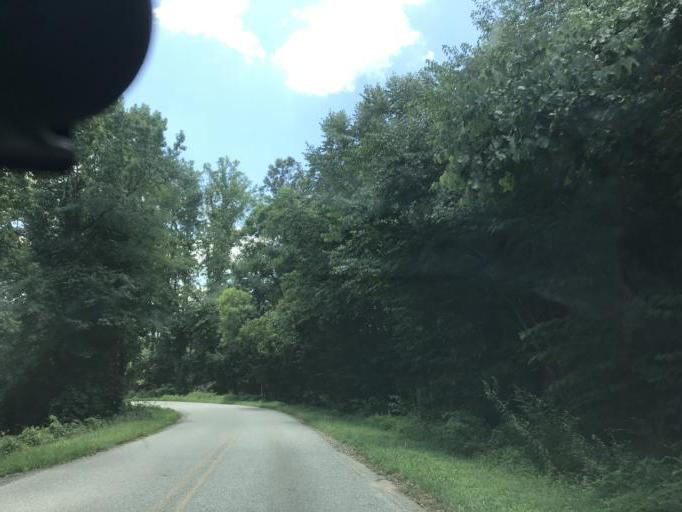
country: US
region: Georgia
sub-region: Fulton County
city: Milton
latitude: 34.1451
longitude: -84.2407
